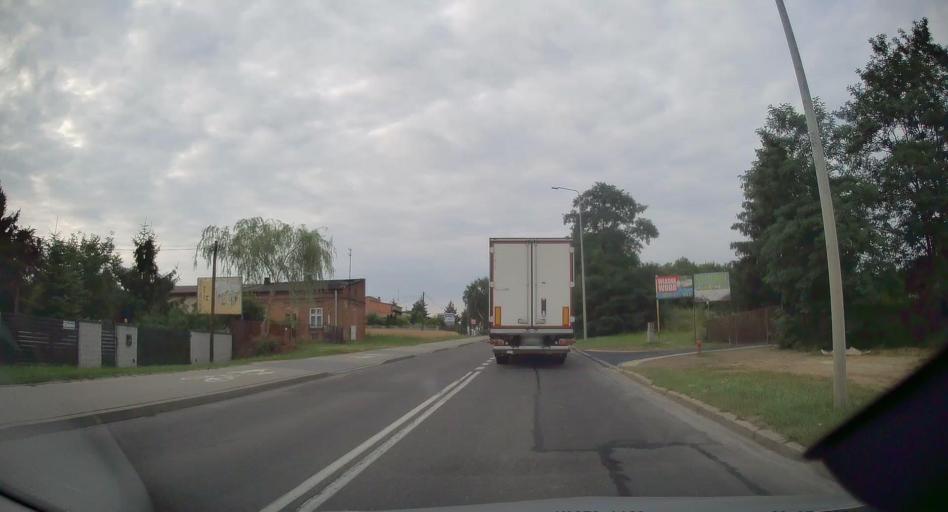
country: PL
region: Lodz Voivodeship
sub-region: Powiat radomszczanski
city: Radomsko
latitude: 51.0507
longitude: 19.4395
